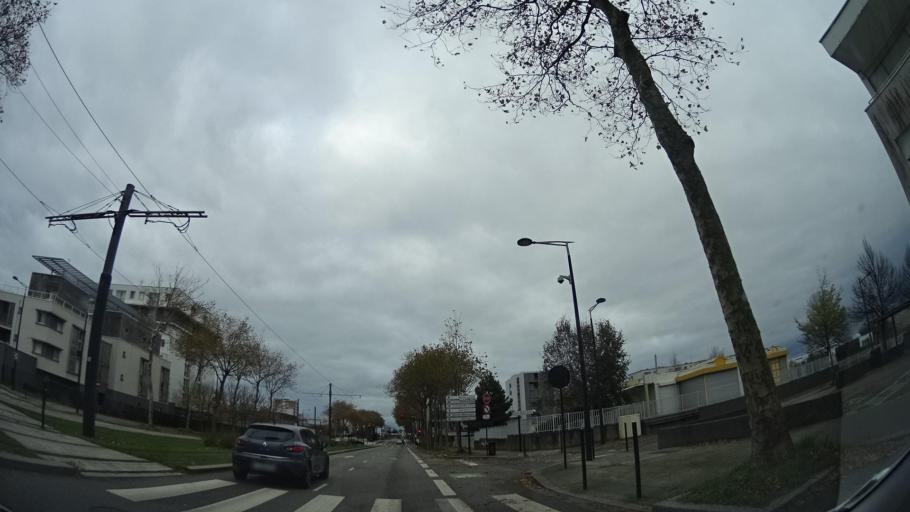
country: FR
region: Haute-Normandie
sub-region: Departement de la Seine-Maritime
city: Le Havre
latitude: 49.5178
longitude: 0.1181
